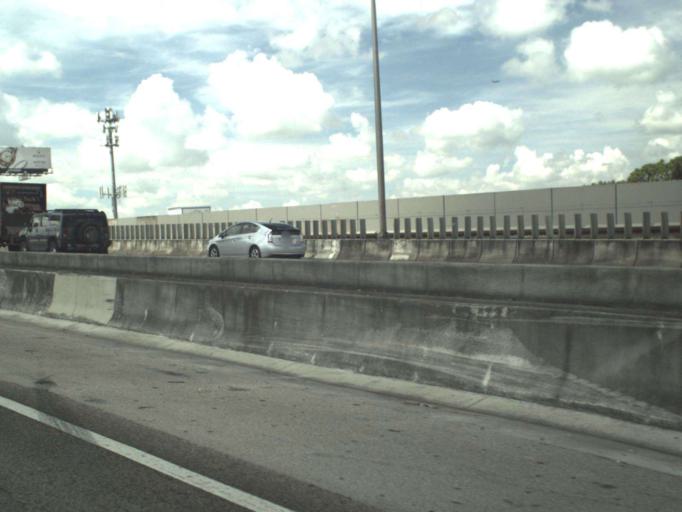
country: US
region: Florida
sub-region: Broward County
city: Boulevard Gardens
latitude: 26.1005
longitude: -80.1691
